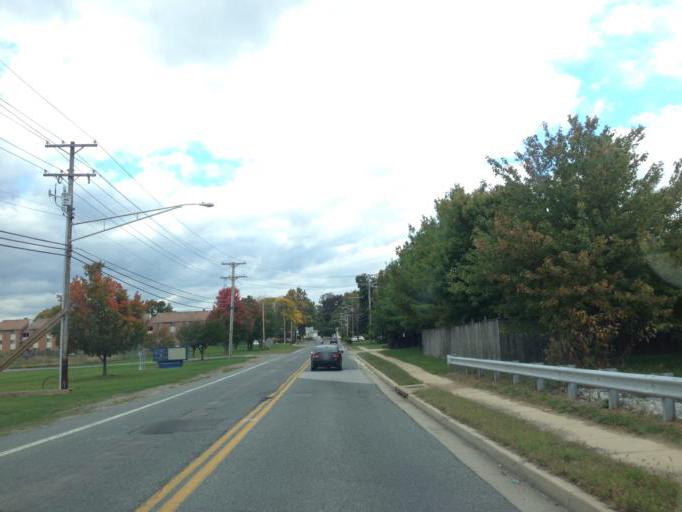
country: US
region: Maryland
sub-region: Baltimore County
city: Milford Mill
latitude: 39.3505
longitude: -76.7661
